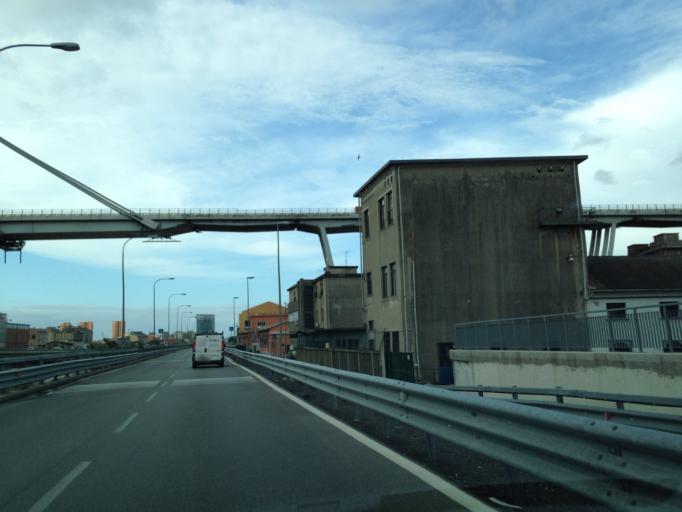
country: IT
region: Liguria
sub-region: Provincia di Genova
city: San Teodoro
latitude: 44.4283
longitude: 8.8887
